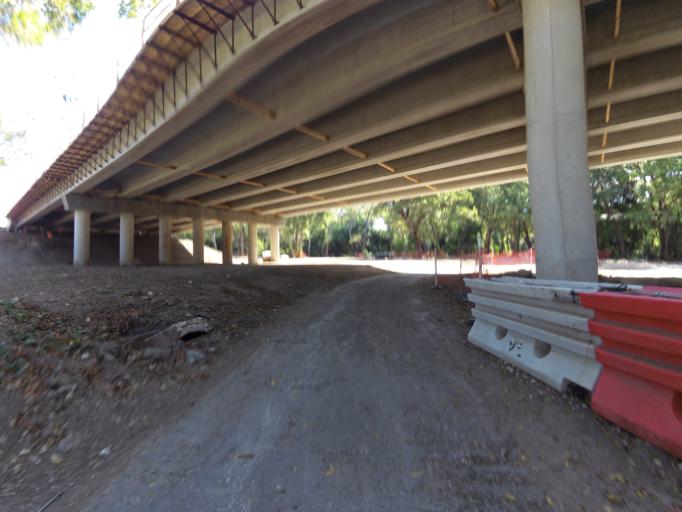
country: US
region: Texas
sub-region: Bexar County
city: Terrell Hills
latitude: 29.4224
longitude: -98.4308
